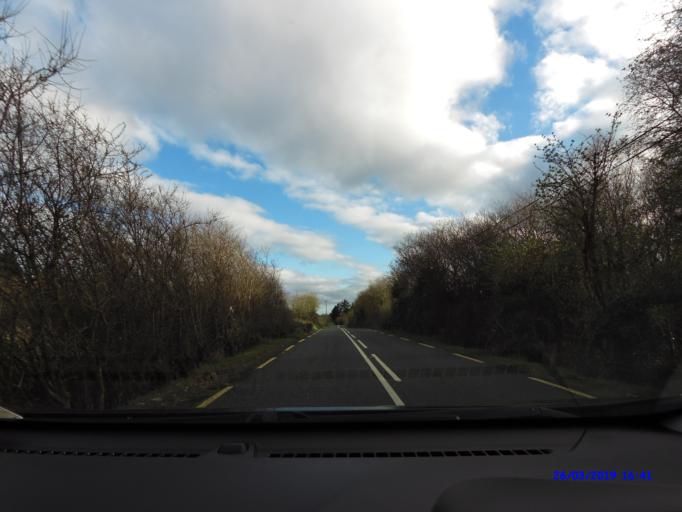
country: IE
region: Connaught
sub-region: Maigh Eo
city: Ballyhaunis
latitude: 53.8735
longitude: -8.7732
